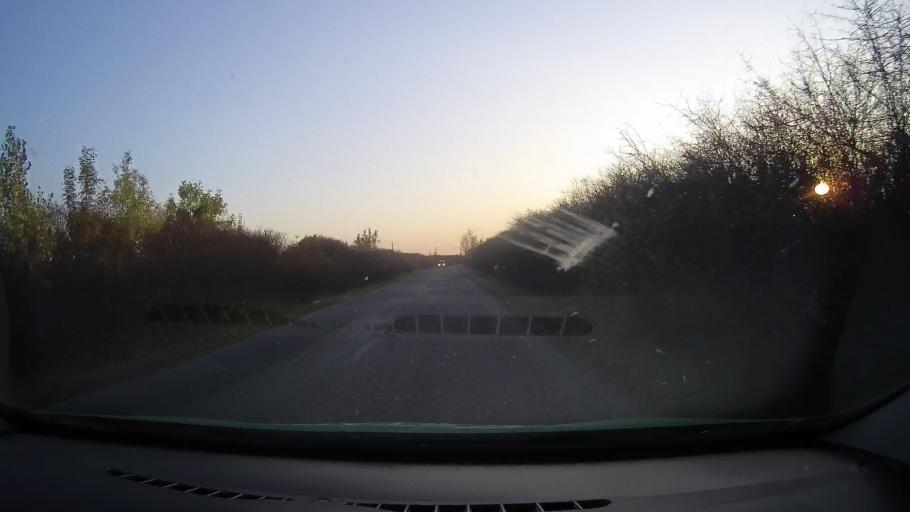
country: RO
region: Arad
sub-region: Comuna Seleus
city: Seleus
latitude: 46.4059
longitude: 21.7294
